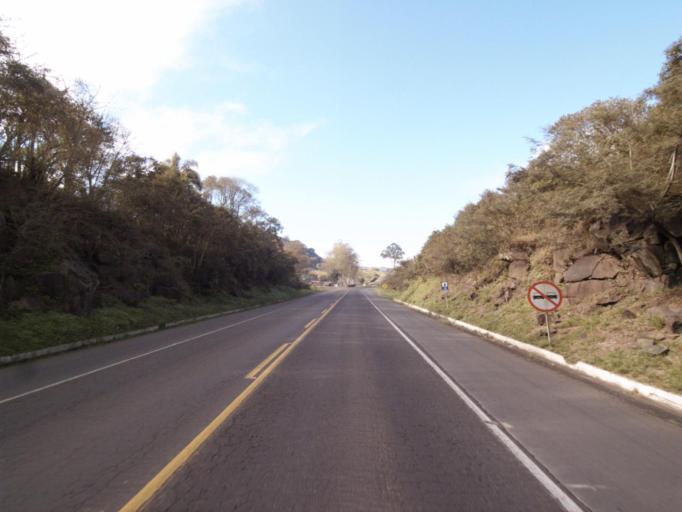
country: BR
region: Rio Grande do Sul
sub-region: Frederico Westphalen
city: Frederico Westphalen
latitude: -27.0351
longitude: -53.2320
